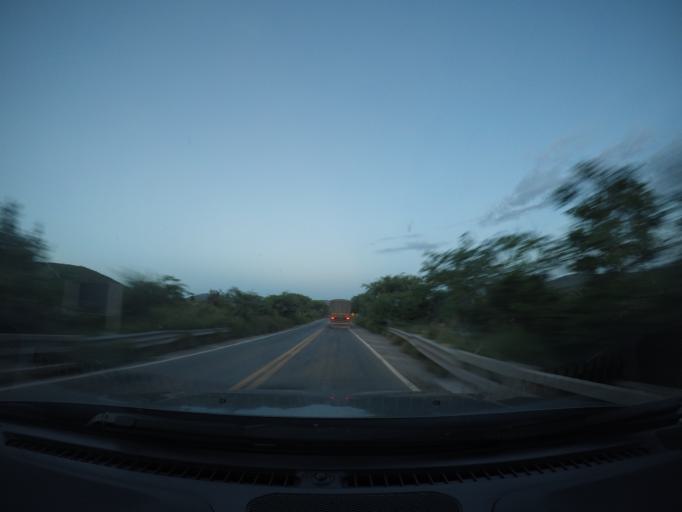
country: BR
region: Bahia
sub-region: Seabra
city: Seabra
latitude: -12.4884
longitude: -41.7293
